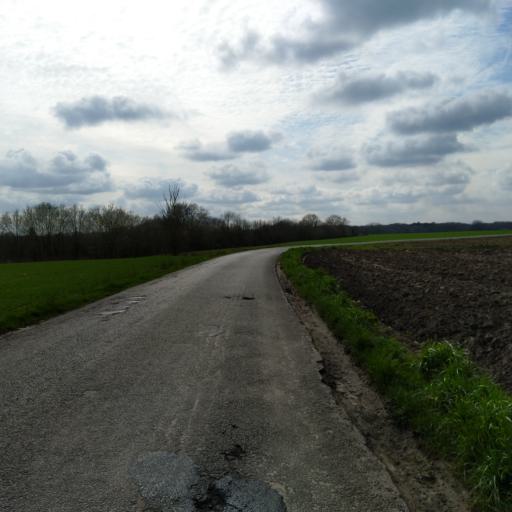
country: BE
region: Wallonia
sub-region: Province du Hainaut
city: Soignies
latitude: 50.5132
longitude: 4.0270
